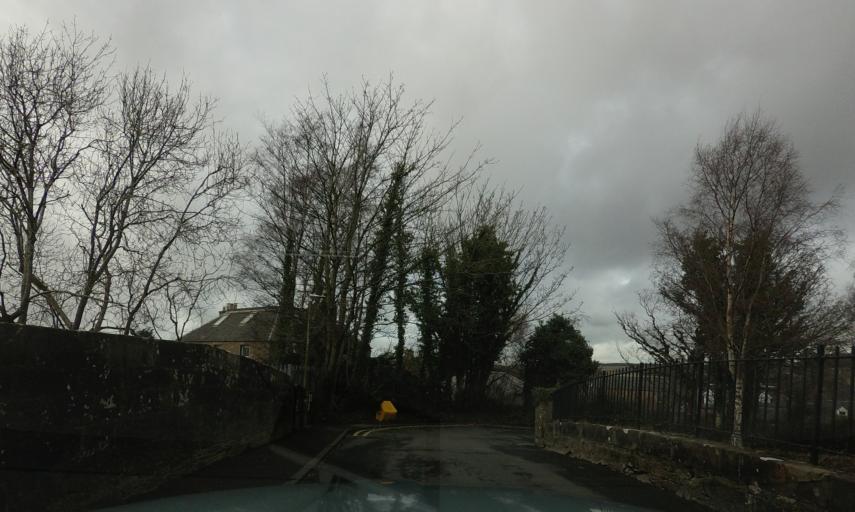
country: GB
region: Scotland
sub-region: West Lothian
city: Linlithgow
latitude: 55.9744
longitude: -3.6026
